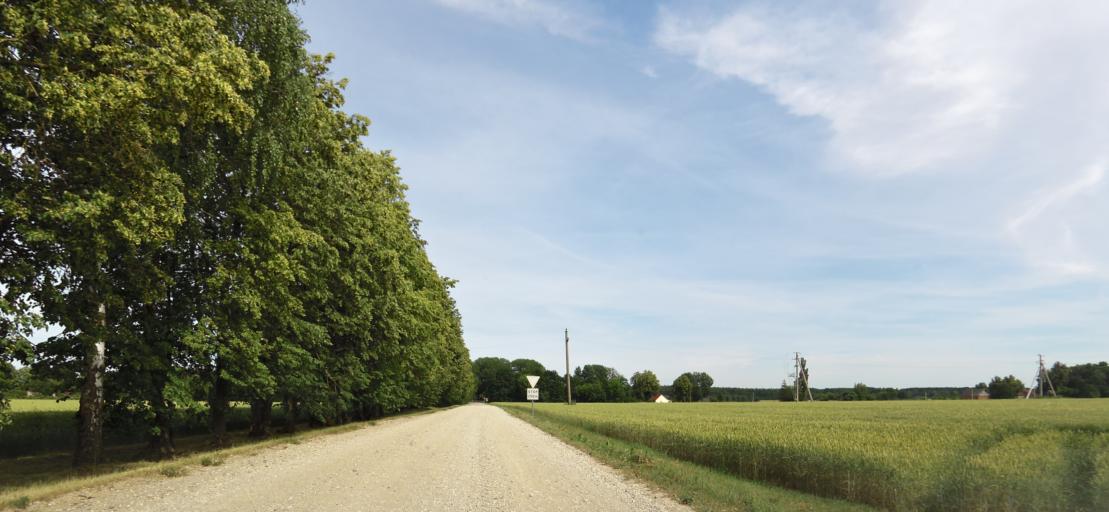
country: LT
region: Panevezys
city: Pasvalys
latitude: 55.9651
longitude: 24.3351
